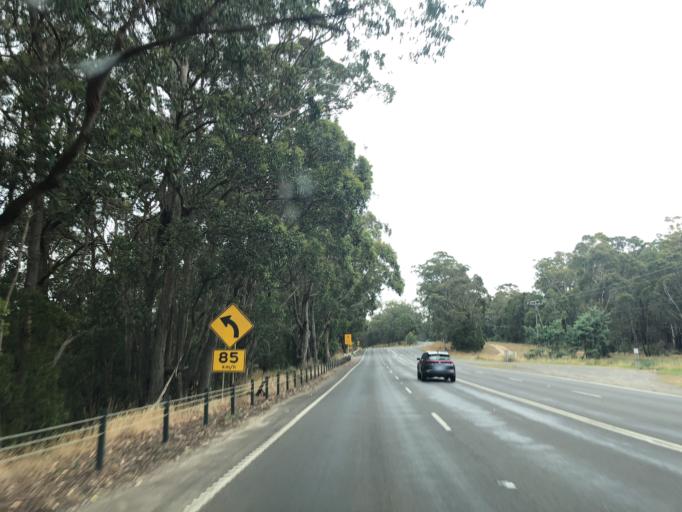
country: AU
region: Victoria
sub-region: Hume
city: Sunbury
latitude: -37.3960
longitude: 144.5287
